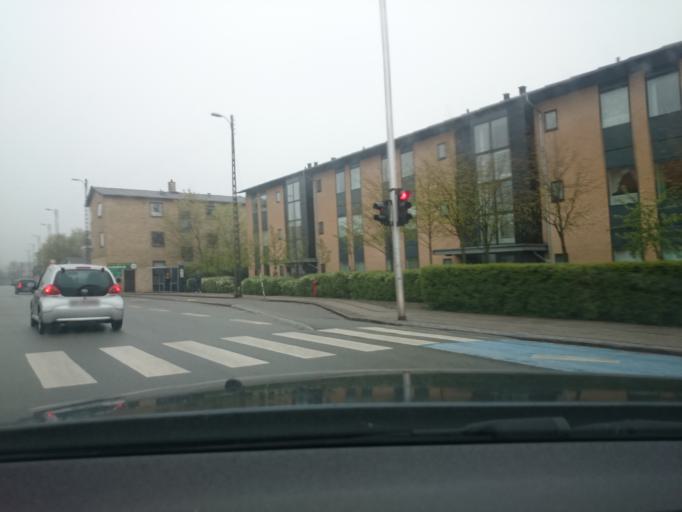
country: DK
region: Capital Region
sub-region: Gladsaxe Municipality
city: Buddinge
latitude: 55.7503
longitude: 12.4952
